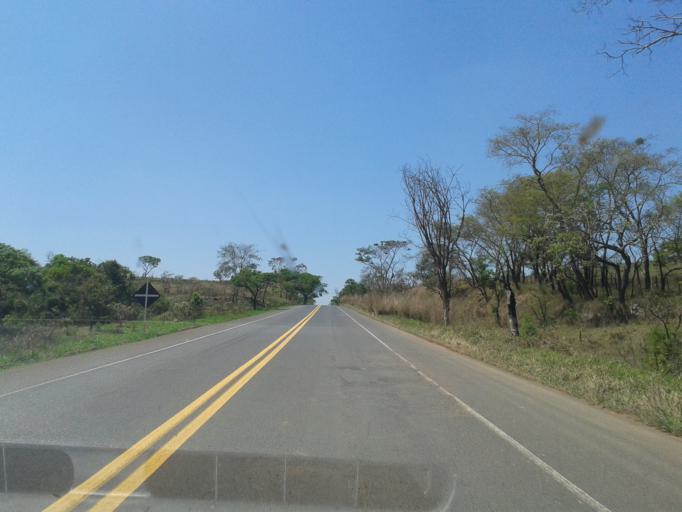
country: BR
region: Minas Gerais
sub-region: Araxa
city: Araxa
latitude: -19.4711
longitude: -47.1636
